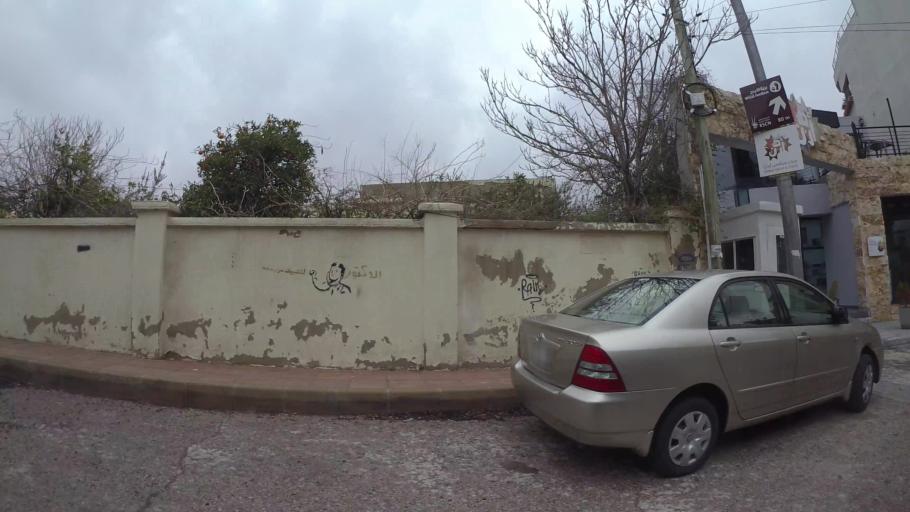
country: JO
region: Amman
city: Amman
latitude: 31.9512
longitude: 35.9301
